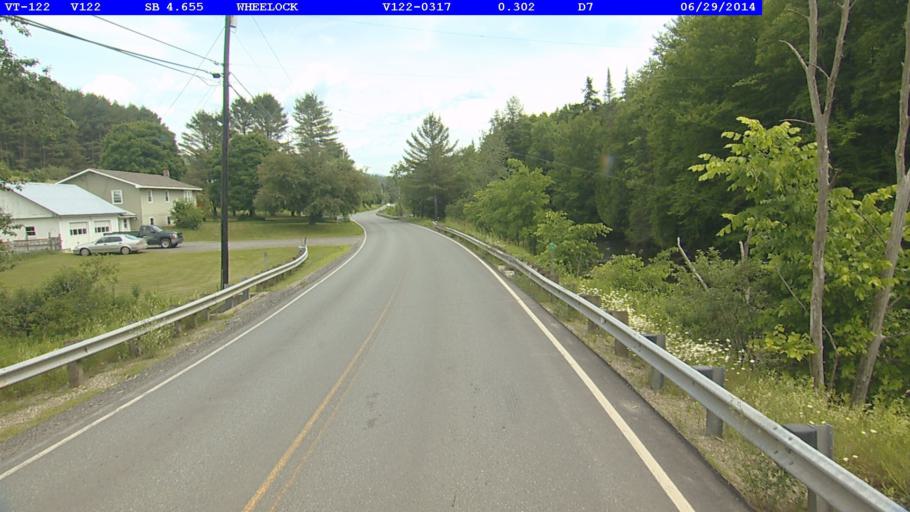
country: US
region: Vermont
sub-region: Caledonia County
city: Lyndonville
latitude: 44.5804
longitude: -72.0695
